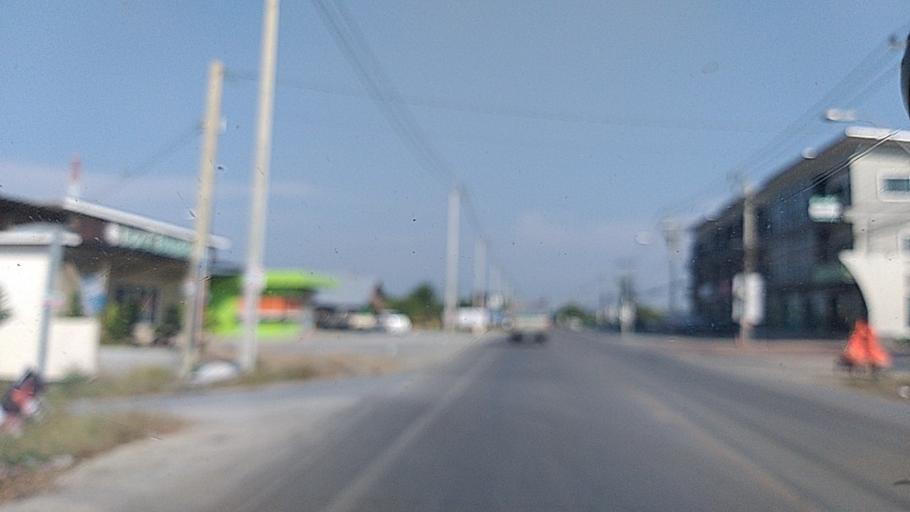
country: TH
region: Nonthaburi
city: Sai Noi
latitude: 13.9453
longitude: 100.3555
